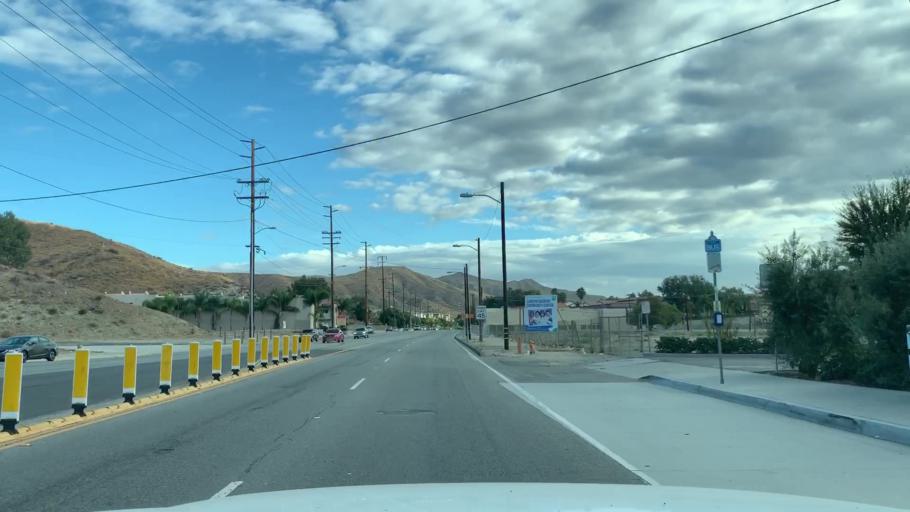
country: US
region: California
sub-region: Los Angeles County
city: Santa Clarita
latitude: 34.4170
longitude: -118.4555
